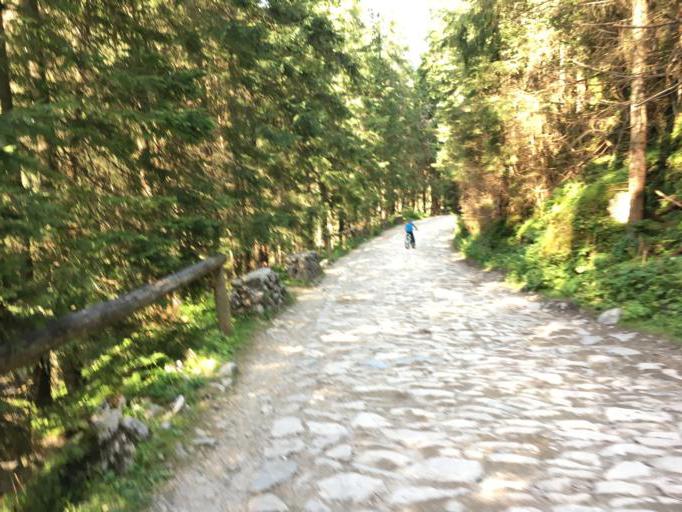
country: PL
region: Lesser Poland Voivodeship
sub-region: Powiat tatrzanski
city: Koscielisko
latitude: 49.2412
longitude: 19.8073
